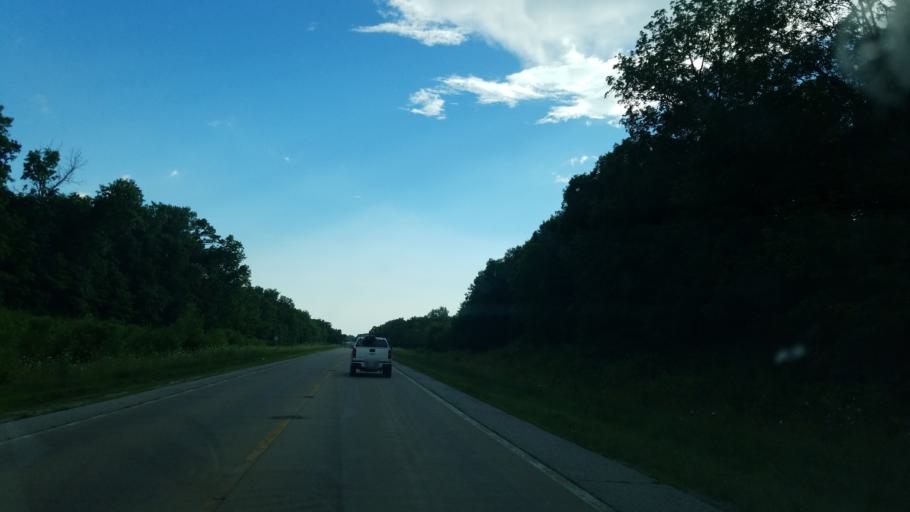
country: US
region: Illinois
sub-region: Marion County
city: Central City
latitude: 38.5675
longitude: -89.1142
